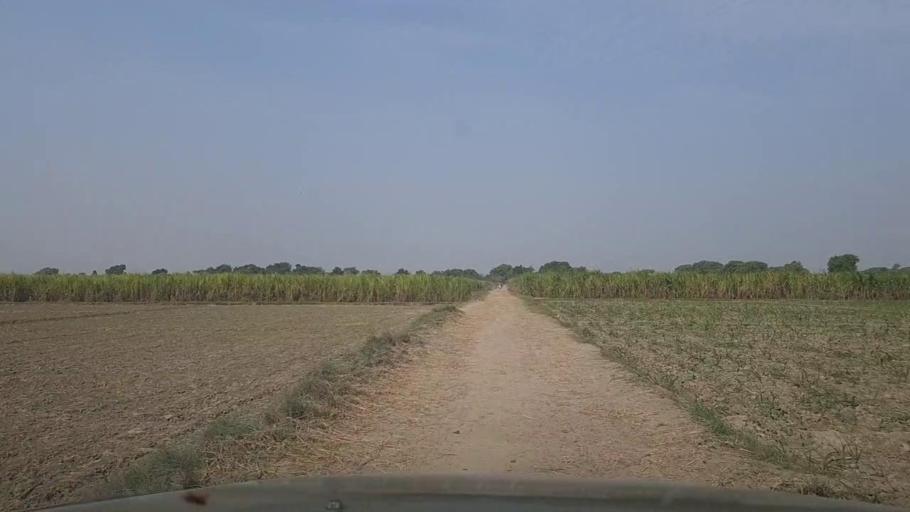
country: PK
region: Sindh
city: Bulri
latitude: 25.0208
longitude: 68.2821
